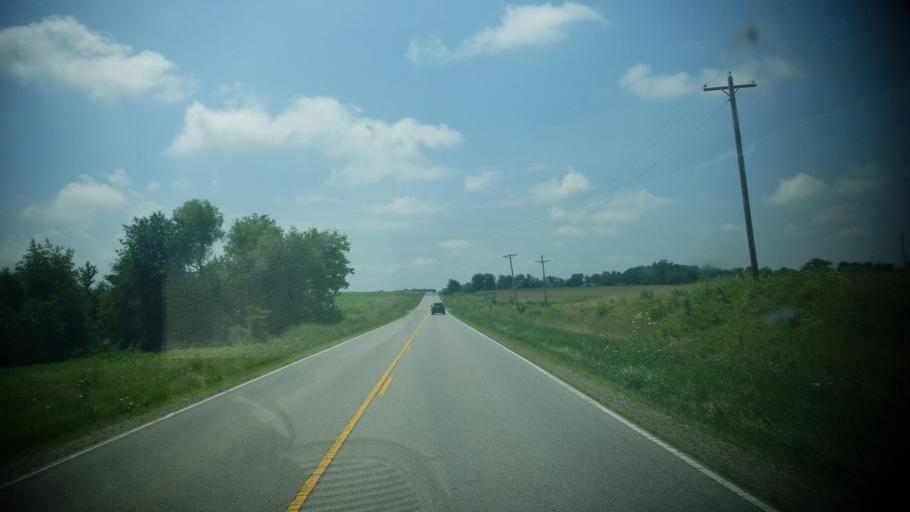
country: US
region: Illinois
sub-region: Wayne County
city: Fairfield
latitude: 38.4313
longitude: -88.3496
